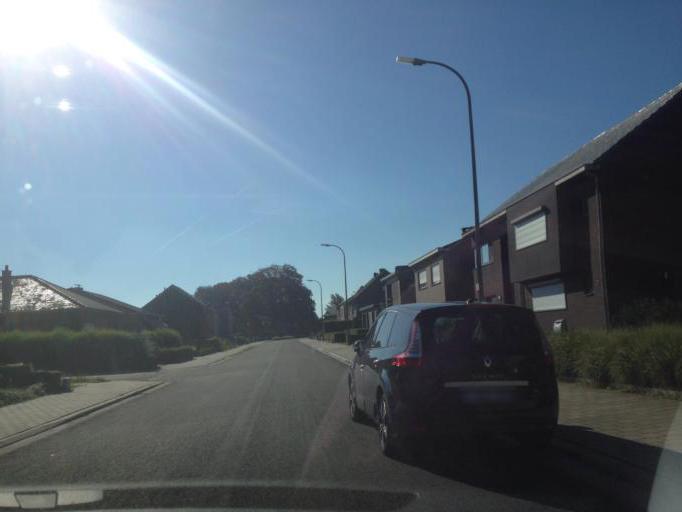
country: BE
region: Flanders
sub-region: Provincie Antwerpen
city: Geel
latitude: 51.1661
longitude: 5.0094
